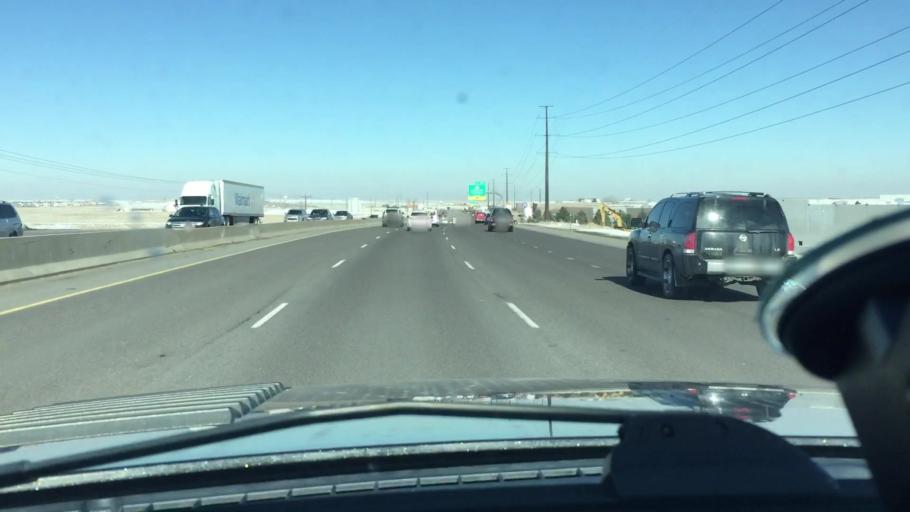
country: US
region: Colorado
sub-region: Boulder County
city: Erie
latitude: 39.9888
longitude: -104.9864
